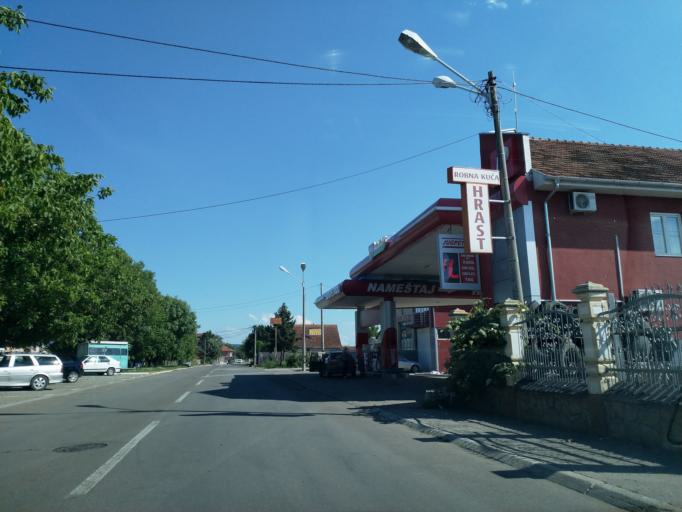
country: RS
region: Central Serbia
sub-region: Pomoravski Okrug
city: Paracin
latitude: 43.8510
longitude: 21.4105
